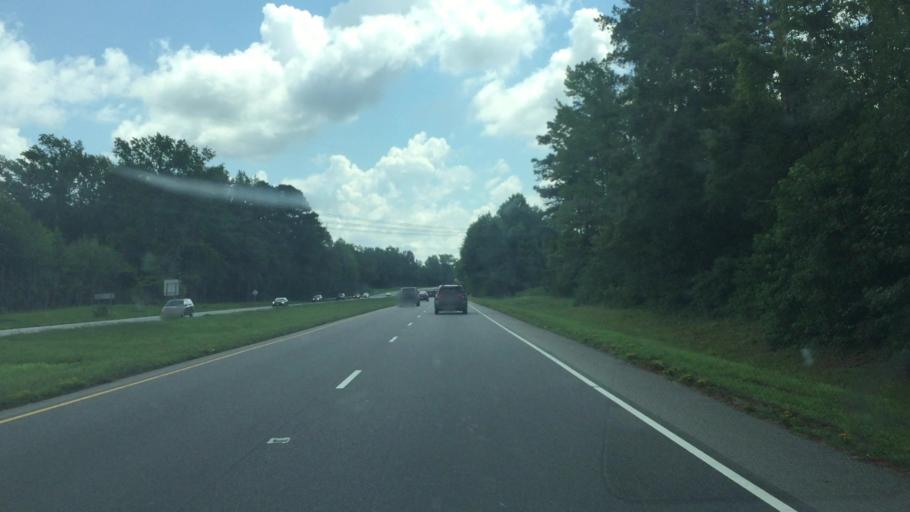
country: US
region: North Carolina
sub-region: Scotland County
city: Laurel Hill
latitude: 34.7992
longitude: -79.5271
